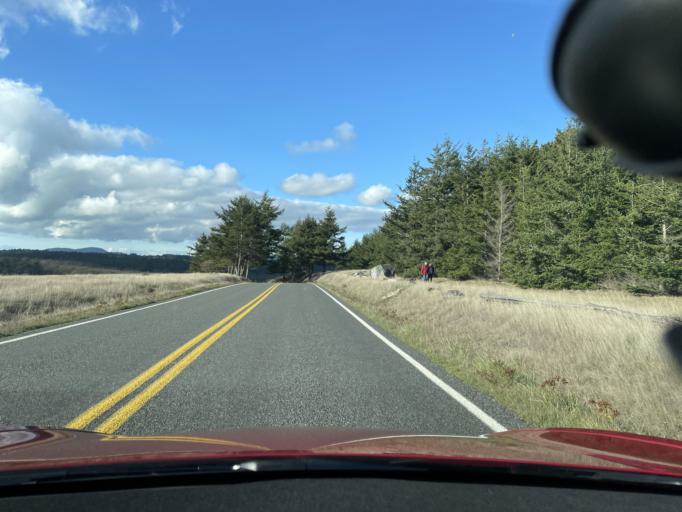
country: US
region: Washington
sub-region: San Juan County
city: Friday Harbor
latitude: 48.4622
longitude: -122.9975
